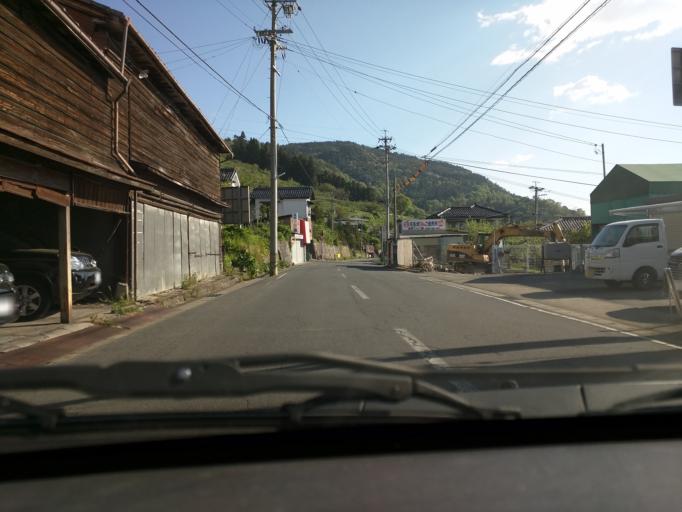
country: JP
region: Nagano
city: Nagano-shi
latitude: 36.6641
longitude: 138.1787
